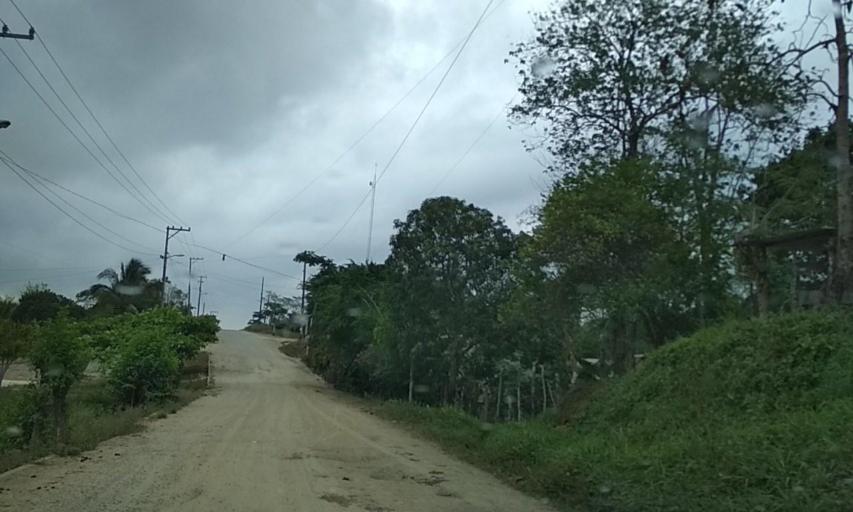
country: MX
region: Tabasco
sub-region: Huimanguillo
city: Francisco Rueda
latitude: 17.6546
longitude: -94.0981
